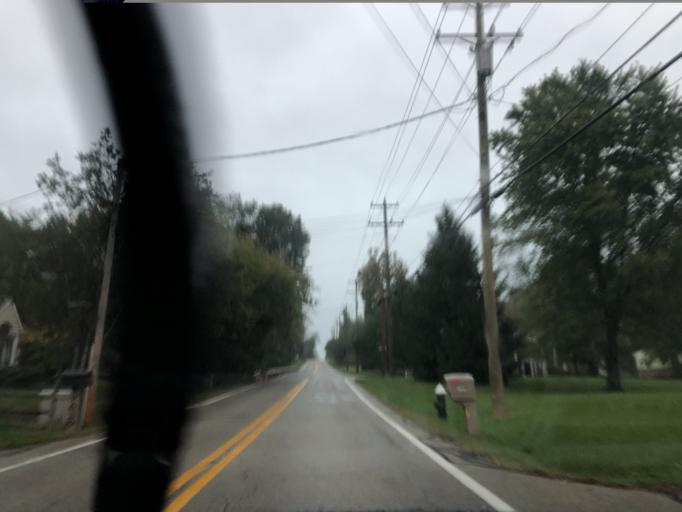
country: US
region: Ohio
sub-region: Hamilton County
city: Montgomery
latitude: 39.2302
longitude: -84.3219
